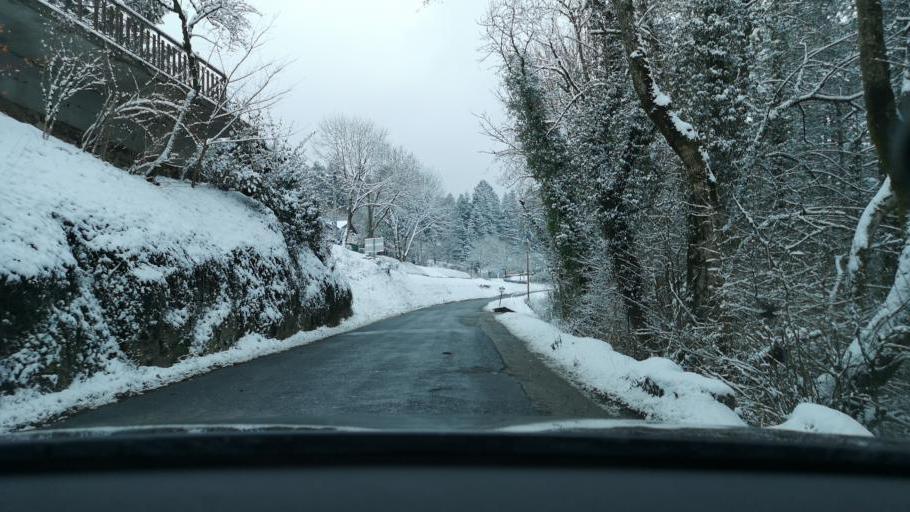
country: FR
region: Rhone-Alpes
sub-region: Departement de l'Ain
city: Oyonnax
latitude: 46.2569
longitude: 5.6647
